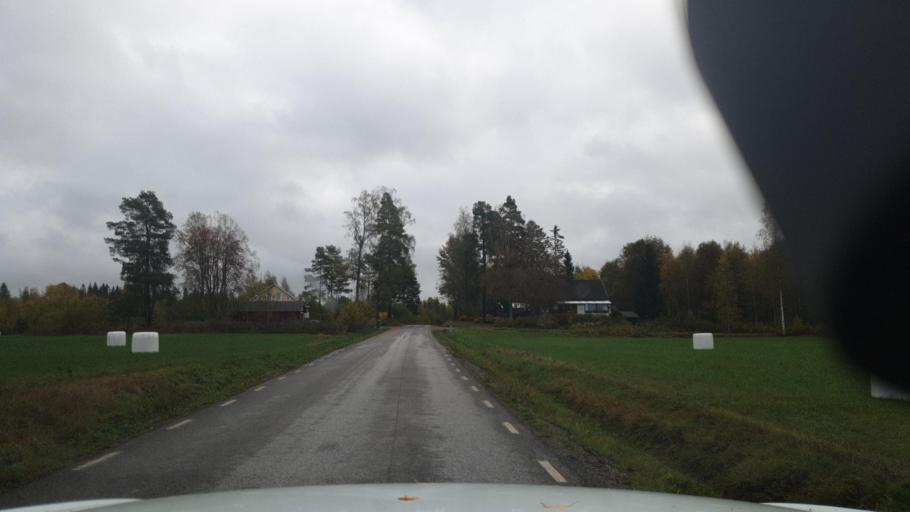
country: SE
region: Vaermland
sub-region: Karlstads Kommun
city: Valberg
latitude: 59.4192
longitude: 13.1134
